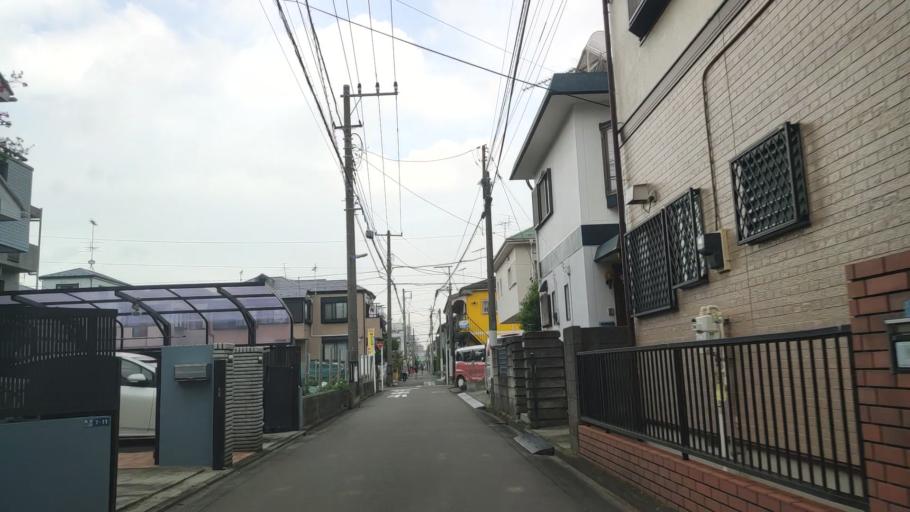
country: JP
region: Kanagawa
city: Minami-rinkan
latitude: 35.4883
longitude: 139.4528
